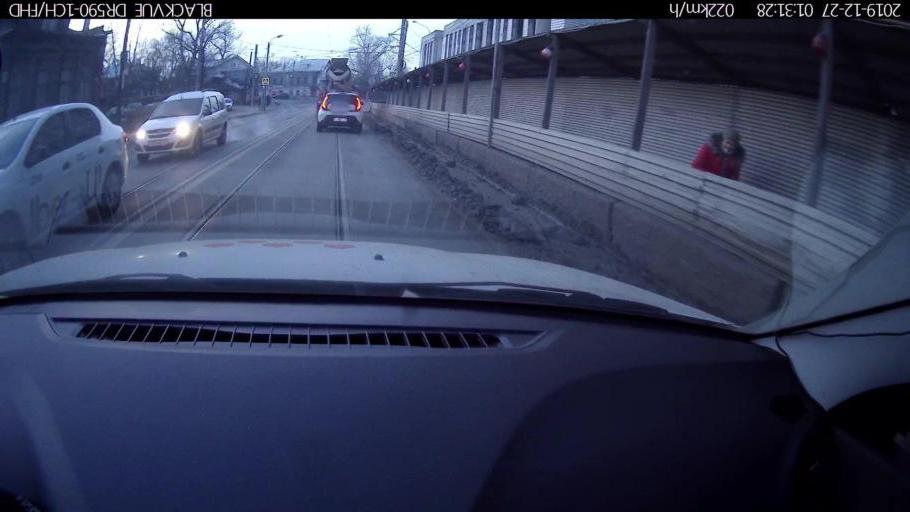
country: RU
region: Nizjnij Novgorod
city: Nizhniy Novgorod
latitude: 56.3156
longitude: 43.9849
